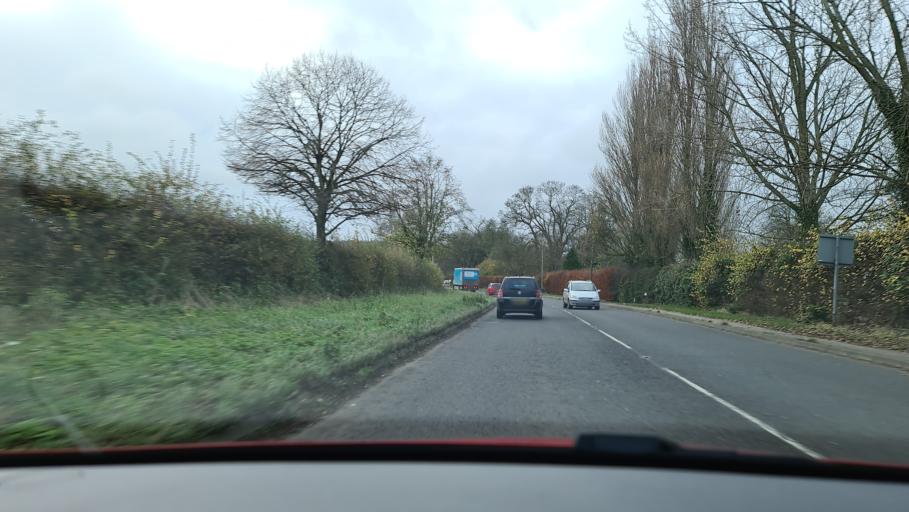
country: GB
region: England
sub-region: Buckinghamshire
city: Weston Turville
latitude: 51.7689
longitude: -0.7881
